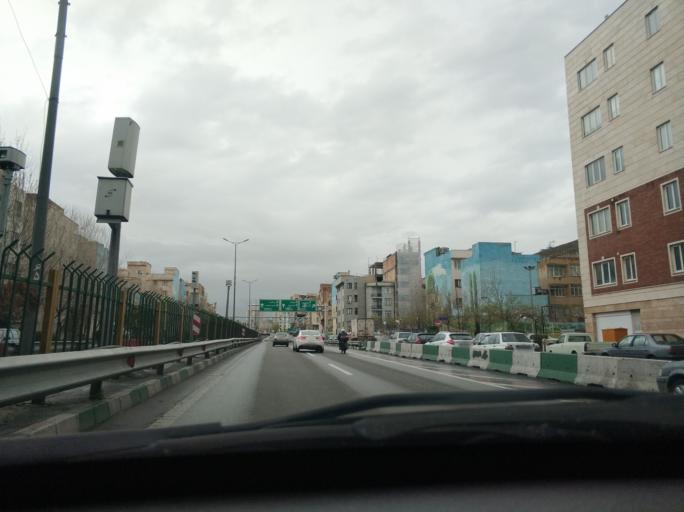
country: IR
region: Tehran
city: Tehran
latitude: 35.7152
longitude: 51.4462
